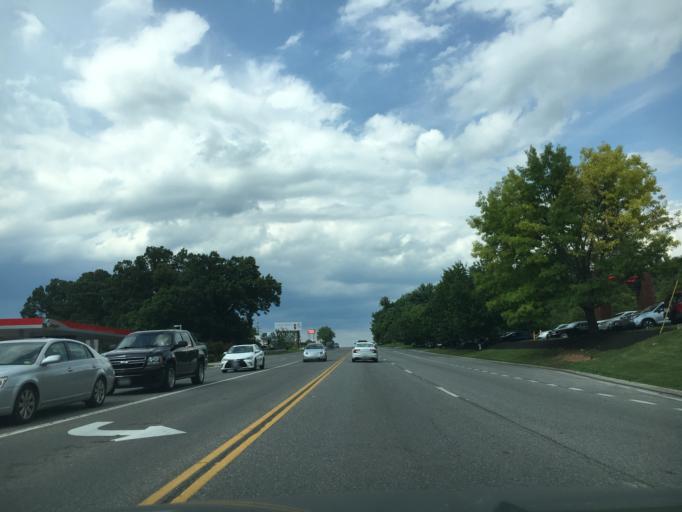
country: US
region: Virginia
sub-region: Roanoke County
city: Cave Spring
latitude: 37.2242
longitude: -80.0131
